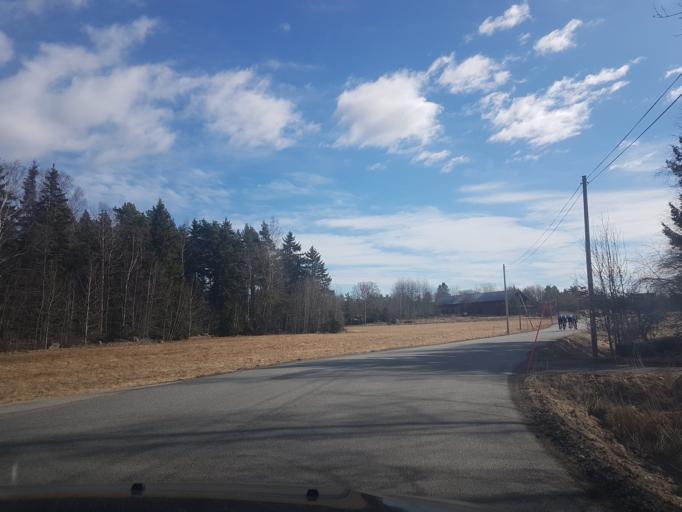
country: SE
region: Stockholm
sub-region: Norrtalje Kommun
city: Nykvarn
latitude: 59.7923
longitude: 18.3180
